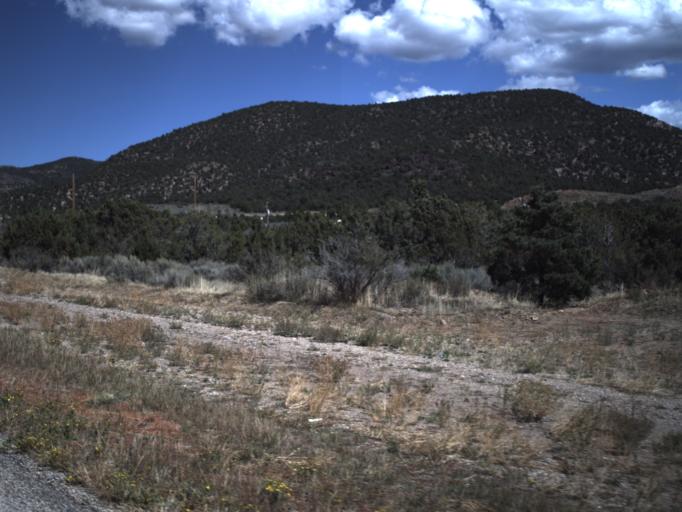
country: US
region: Utah
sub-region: Washington County
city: Enterprise
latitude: 37.4226
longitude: -113.6308
